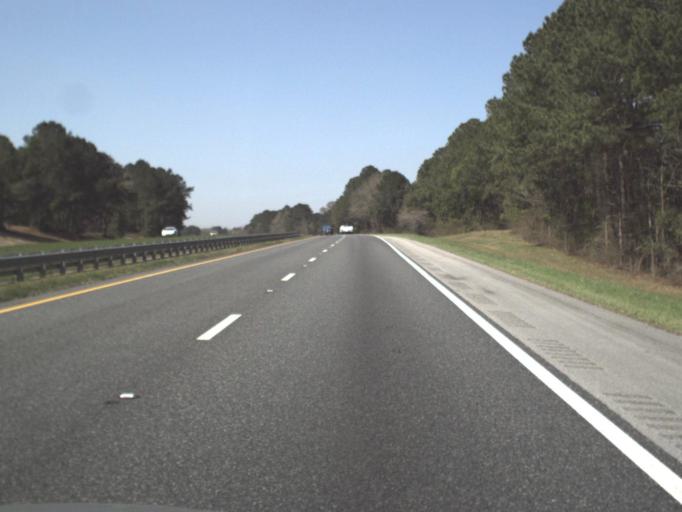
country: US
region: Florida
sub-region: Jackson County
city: Marianna
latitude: 30.7583
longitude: -85.3112
